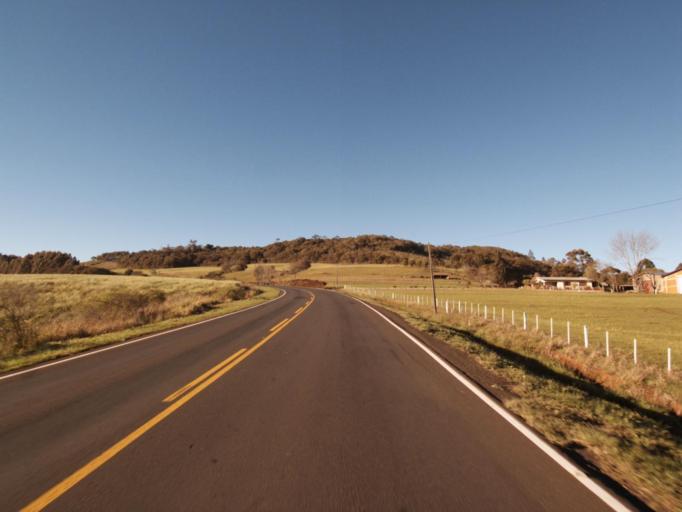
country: AR
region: Misiones
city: Bernardo de Irigoyen
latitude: -26.3539
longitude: -53.5437
